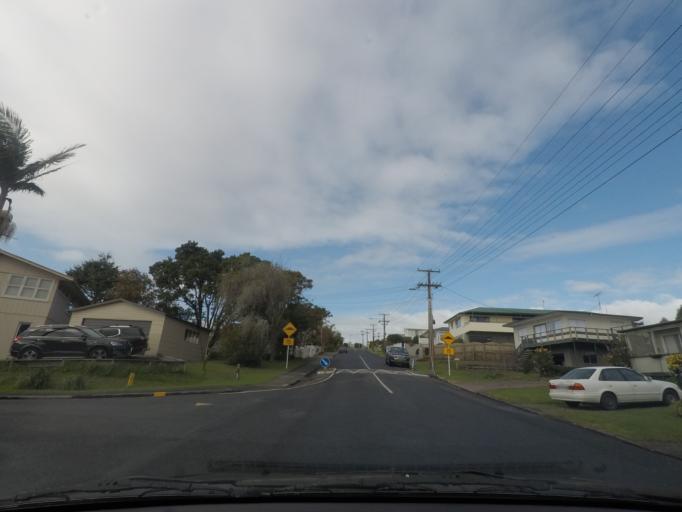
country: NZ
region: Auckland
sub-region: Auckland
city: Warkworth
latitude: -36.4249
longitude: 174.7302
